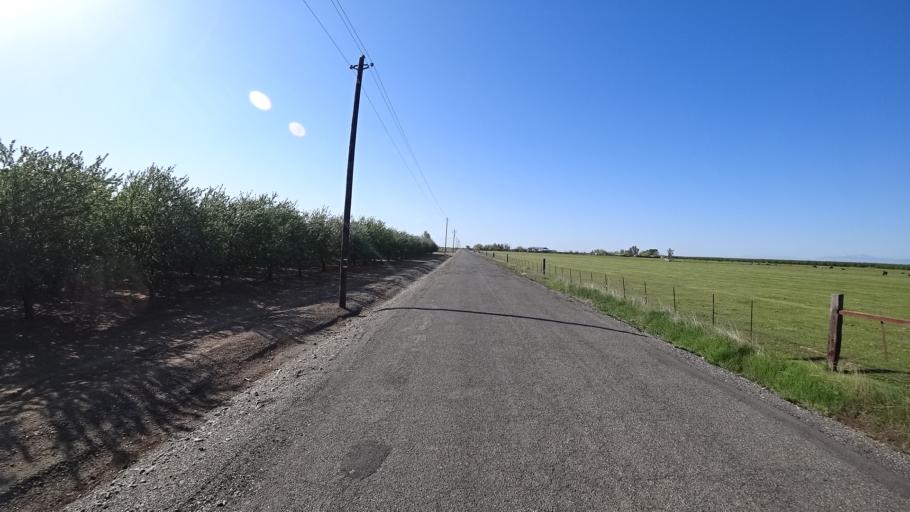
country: US
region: California
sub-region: Glenn County
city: Hamilton City
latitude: 39.7736
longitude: -122.0666
